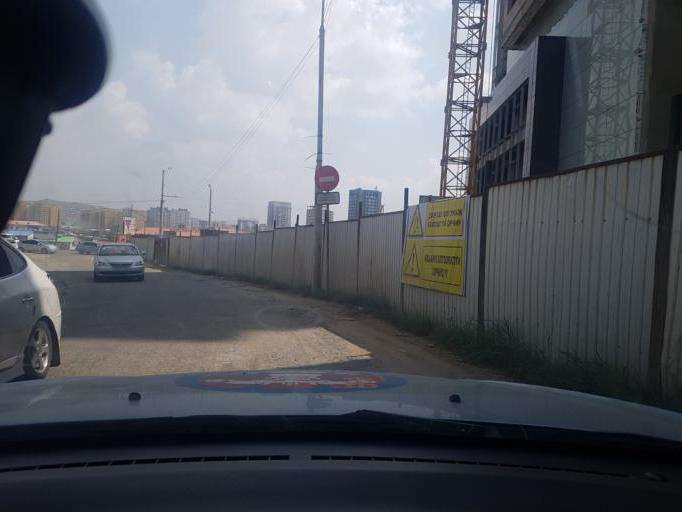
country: MN
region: Ulaanbaatar
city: Ulaanbaatar
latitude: 47.9349
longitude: 106.9064
